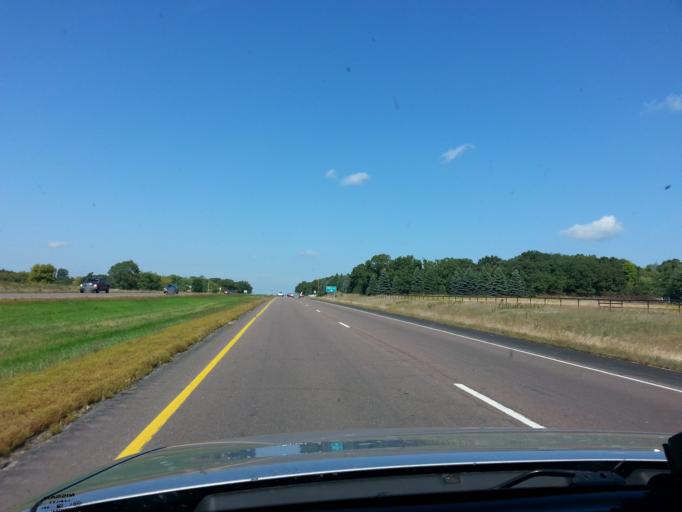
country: US
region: Minnesota
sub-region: Dakota County
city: Rosemount
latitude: 44.6855
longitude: -93.0192
